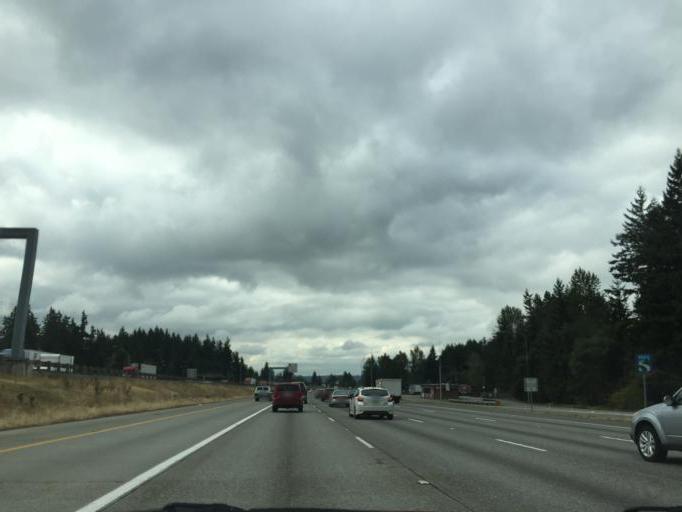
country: US
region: Washington
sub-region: Pierce County
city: Milton
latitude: 47.2745
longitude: -122.3138
